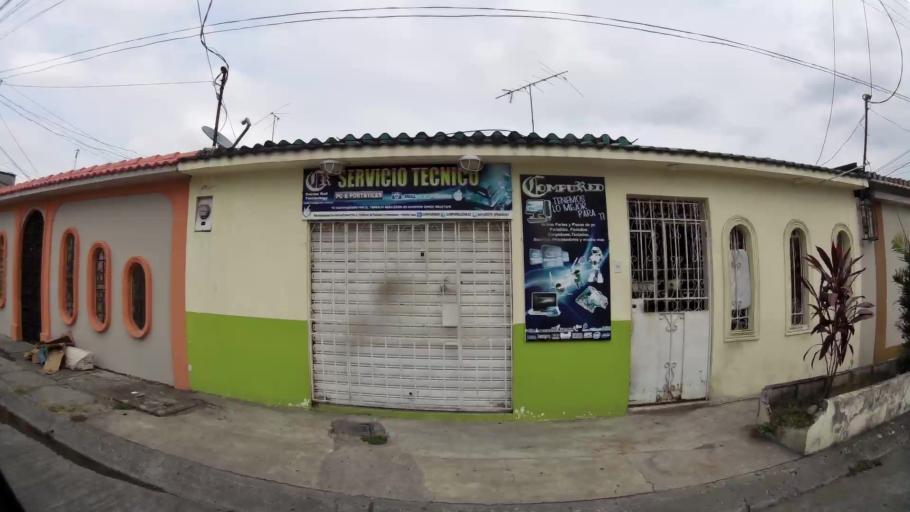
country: EC
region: Guayas
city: Eloy Alfaro
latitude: -2.1200
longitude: -79.8971
